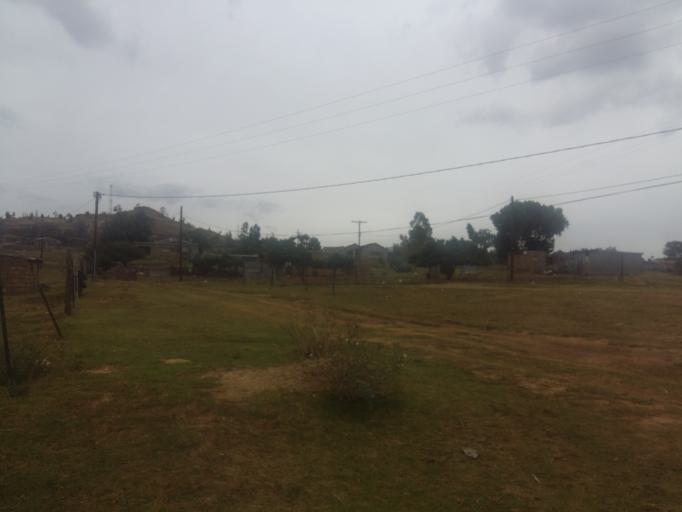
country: LS
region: Mafeteng
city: Mafeteng
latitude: -29.6994
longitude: 27.4341
